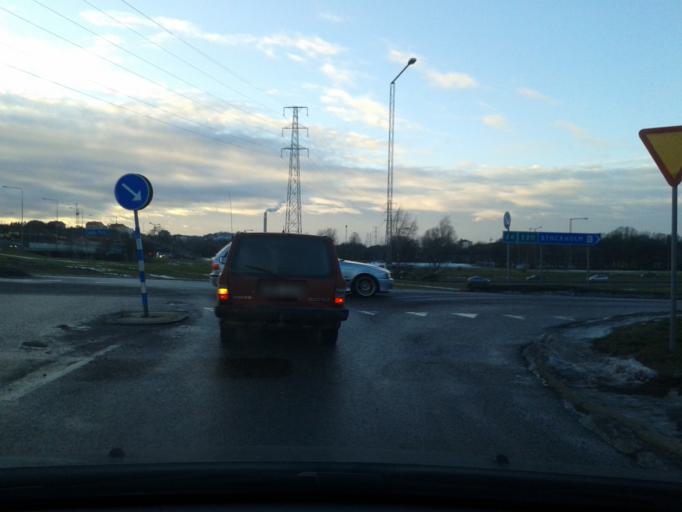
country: SE
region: Stockholm
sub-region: Stockholms Kommun
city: Arsta
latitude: 59.2615
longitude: 18.1018
